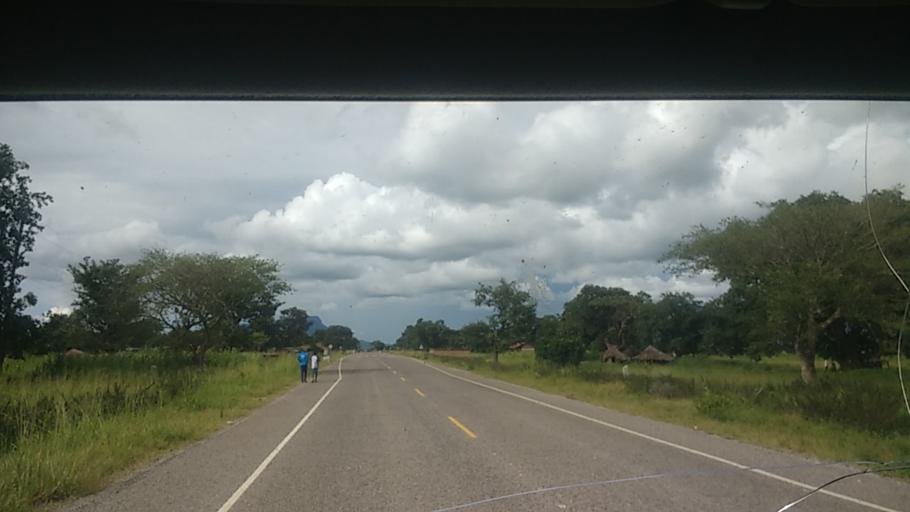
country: UG
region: Eastern Region
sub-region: Katakwi District
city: Katakwi
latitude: 2.0208
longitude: 34.1148
